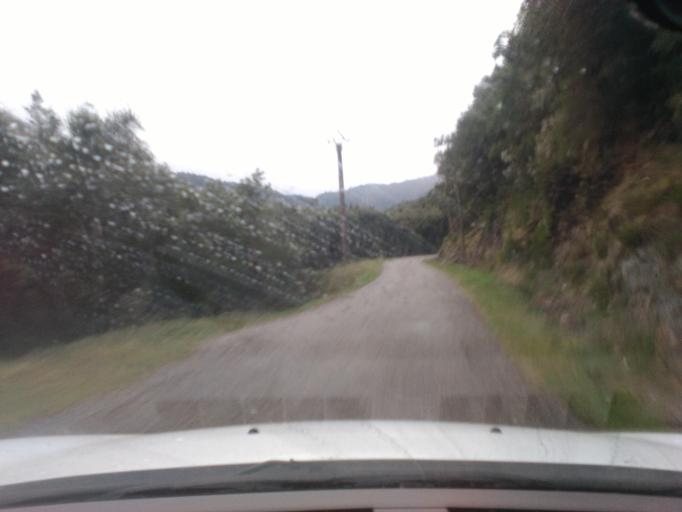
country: FR
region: Languedoc-Roussillon
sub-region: Departement du Gard
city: Valleraugue
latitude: 44.1070
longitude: 3.6785
